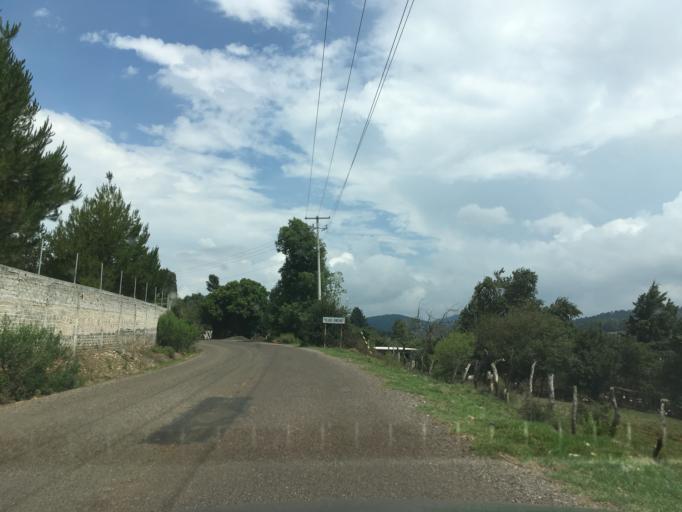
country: MX
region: Michoacan
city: Acuitzio del Canje
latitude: 19.5088
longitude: -101.2498
